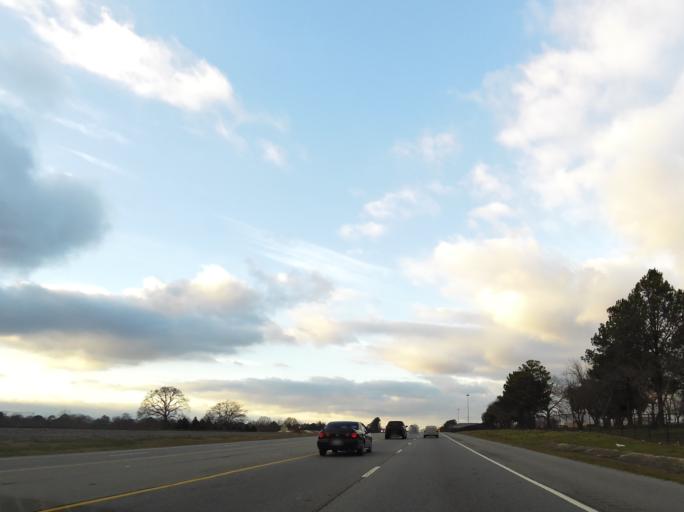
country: US
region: Georgia
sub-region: Houston County
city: Robins Air Force Base
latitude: 32.6075
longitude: -83.5954
